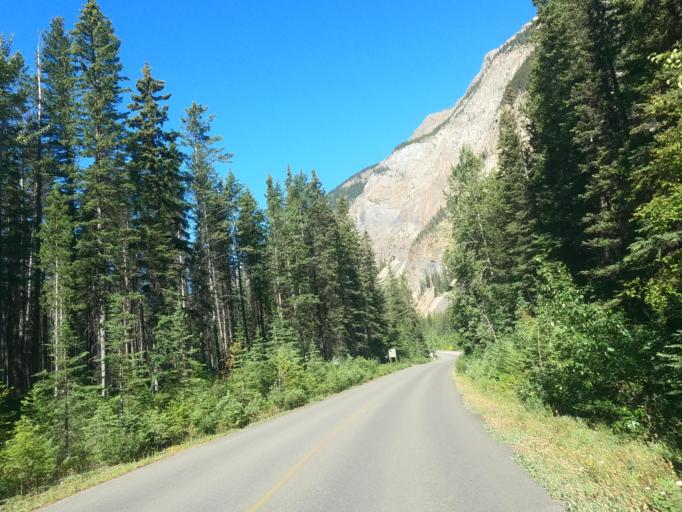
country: CA
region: Alberta
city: Lake Louise
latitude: 51.4227
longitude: -116.4330
